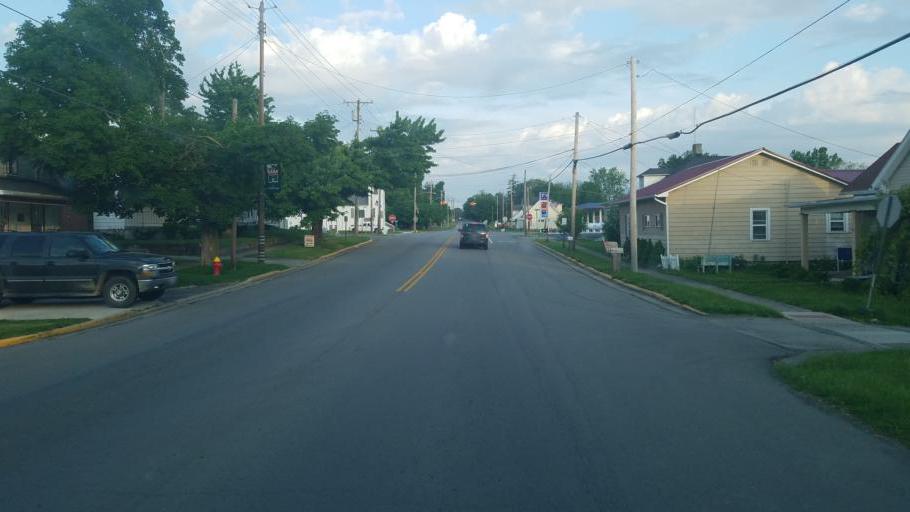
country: US
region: Ohio
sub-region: Highland County
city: Leesburg
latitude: 39.3455
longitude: -83.5585
